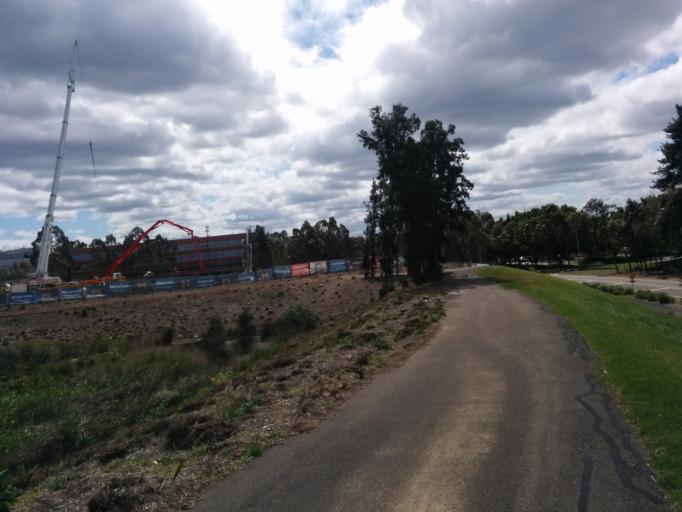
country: AU
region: New South Wales
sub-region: Canada Bay
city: Concord West
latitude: -33.8489
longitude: 151.0747
